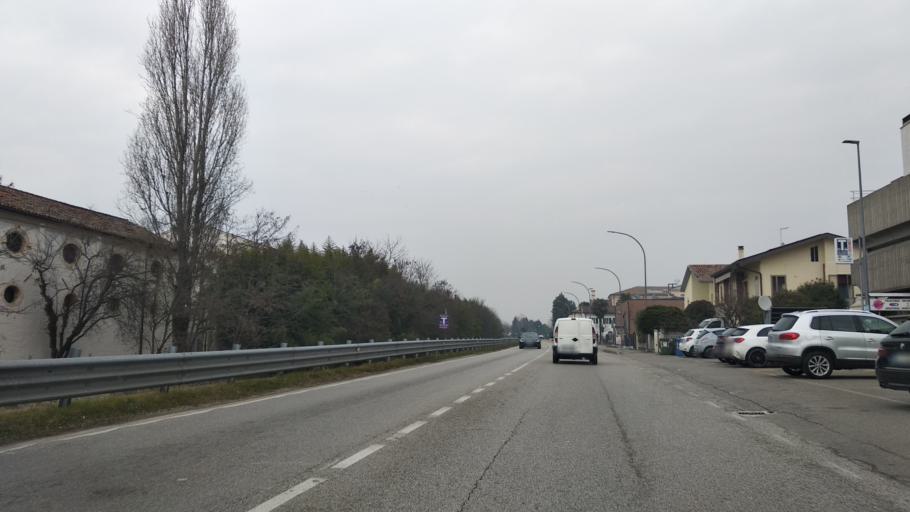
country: IT
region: Veneto
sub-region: Provincia di Padova
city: San Giorgio delle Pertiche
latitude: 45.5409
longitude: 11.8745
